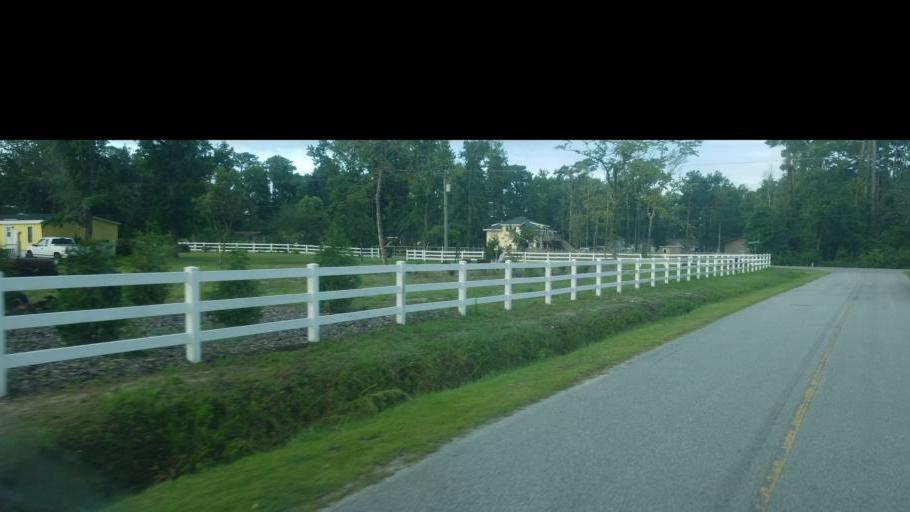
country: US
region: North Carolina
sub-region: Dare County
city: Wanchese
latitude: 35.8438
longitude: -75.6514
